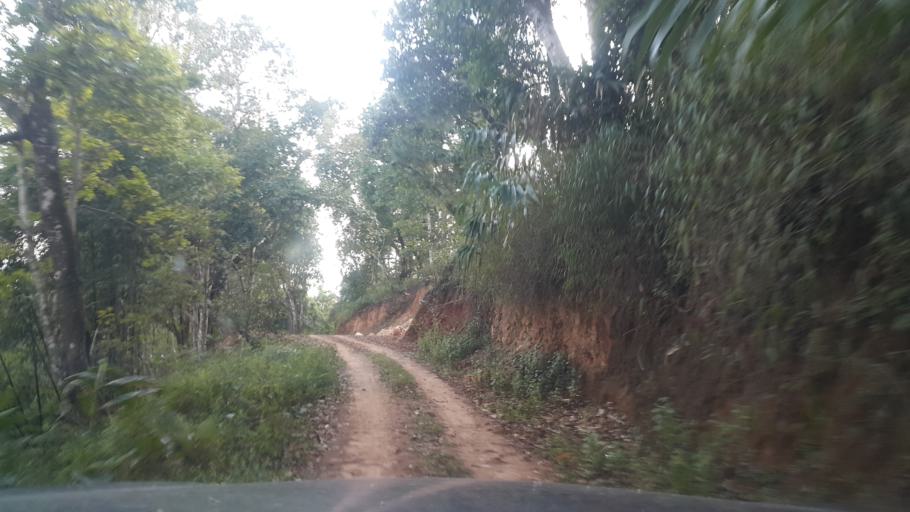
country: TH
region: Chiang Mai
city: Samoeng
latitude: 19.0303
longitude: 98.6474
